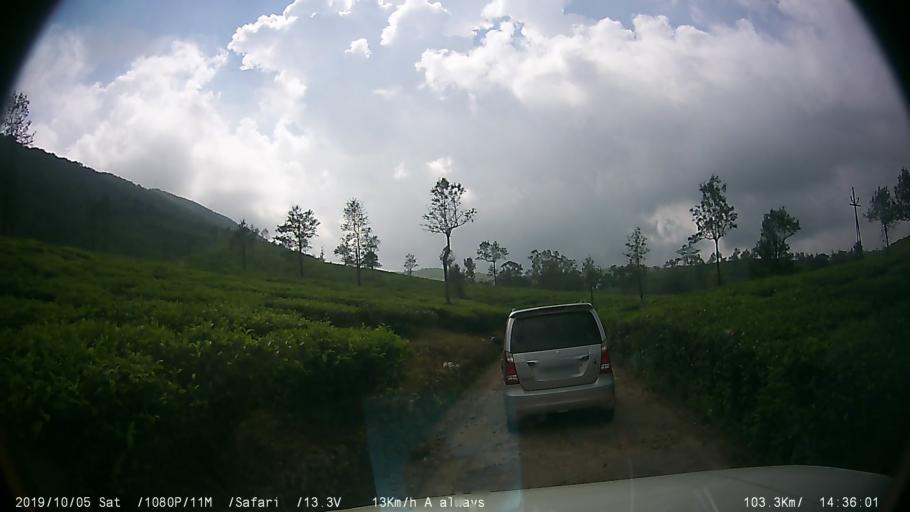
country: IN
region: Kerala
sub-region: Kottayam
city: Erattupetta
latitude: 9.6175
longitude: 76.9616
